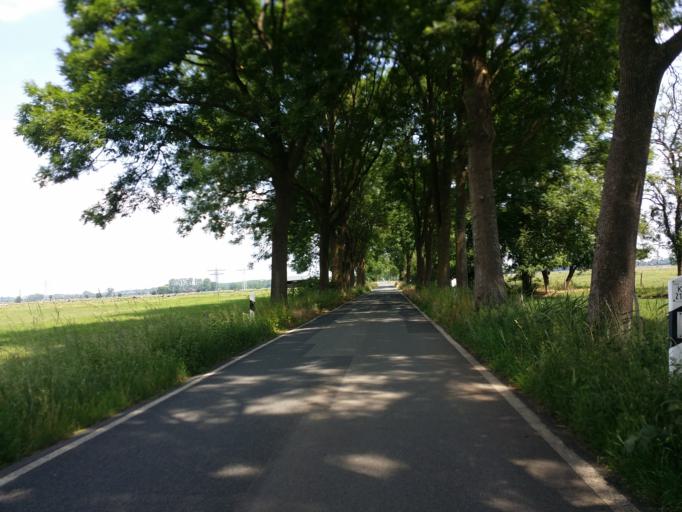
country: DE
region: Lower Saxony
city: Lemwerder
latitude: 53.1423
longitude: 8.5756
